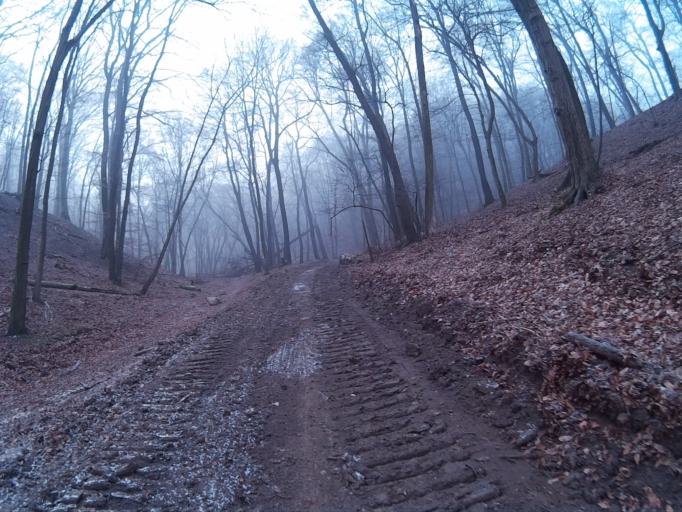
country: HU
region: Fejer
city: Csakvar
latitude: 47.4516
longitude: 18.3966
